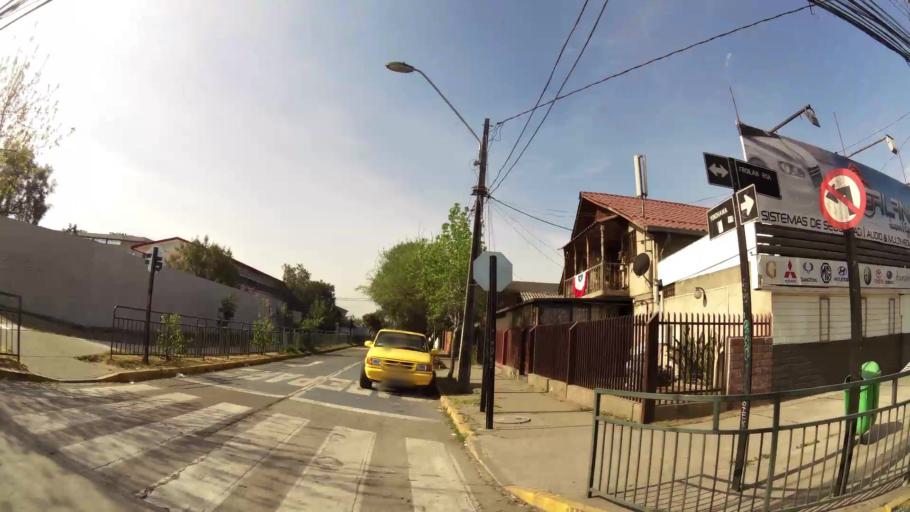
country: CL
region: Santiago Metropolitan
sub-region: Provincia de Santiago
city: Villa Presidente Frei, Nunoa, Santiago, Chile
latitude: -33.5187
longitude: -70.5930
